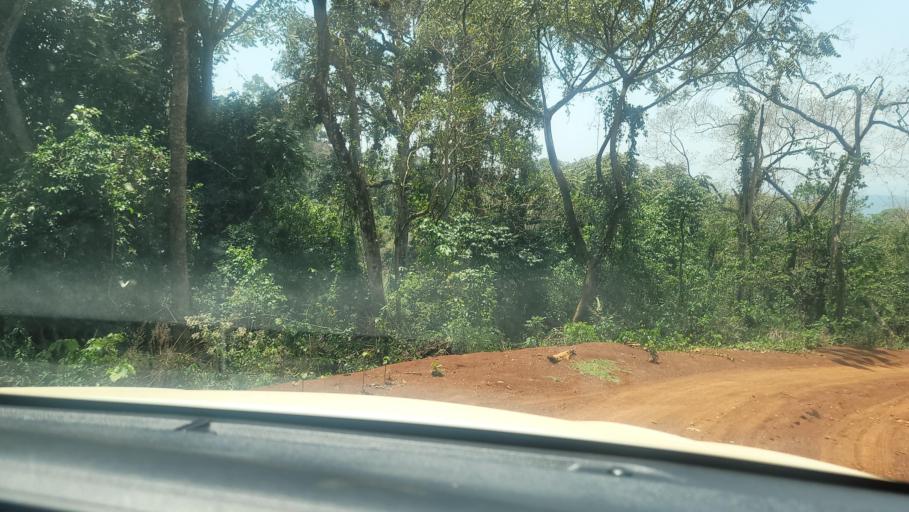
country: ET
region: Southern Nations, Nationalities, and People's Region
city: Bonga
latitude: 7.5467
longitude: 36.1773
